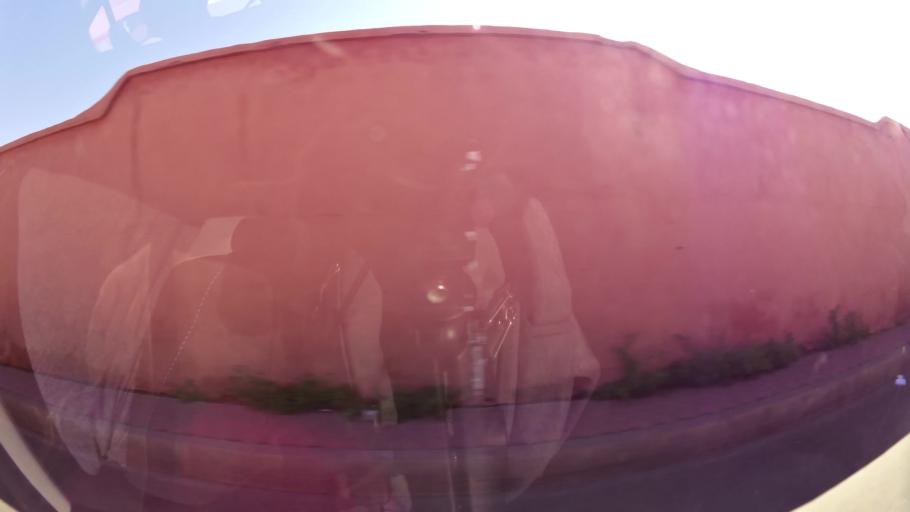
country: MA
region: Marrakech-Tensift-Al Haouz
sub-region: Marrakech
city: Marrakesh
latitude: 31.6367
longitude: -8.0047
